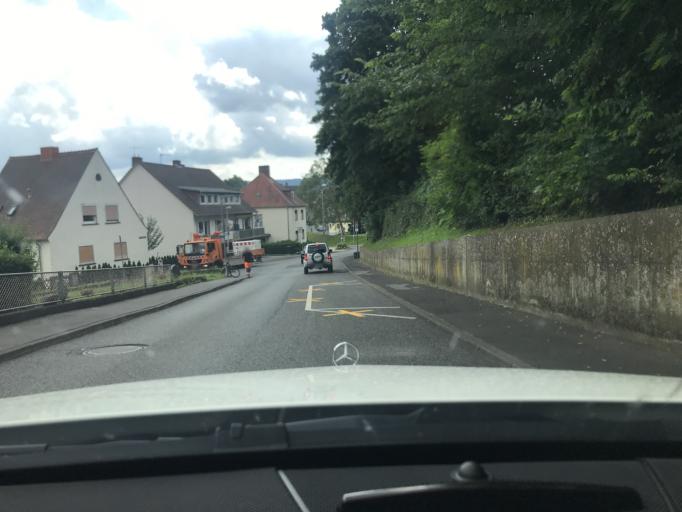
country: DE
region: Hesse
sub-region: Regierungsbezirk Kassel
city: Bad Hersfeld
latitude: 50.8710
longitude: 9.7030
